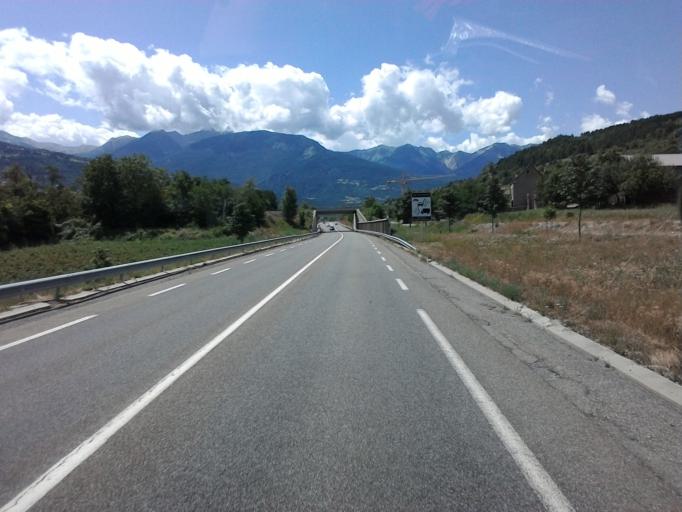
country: FR
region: Provence-Alpes-Cote d'Azur
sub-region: Departement des Hautes-Alpes
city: Embrun
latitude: 44.5850
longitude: 6.5129
